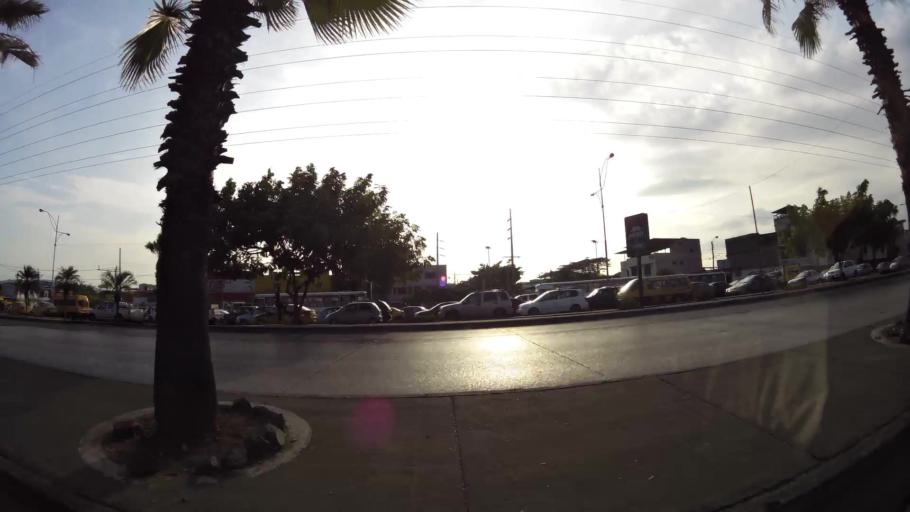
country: EC
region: Guayas
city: Eloy Alfaro
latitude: -2.1315
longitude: -79.9073
